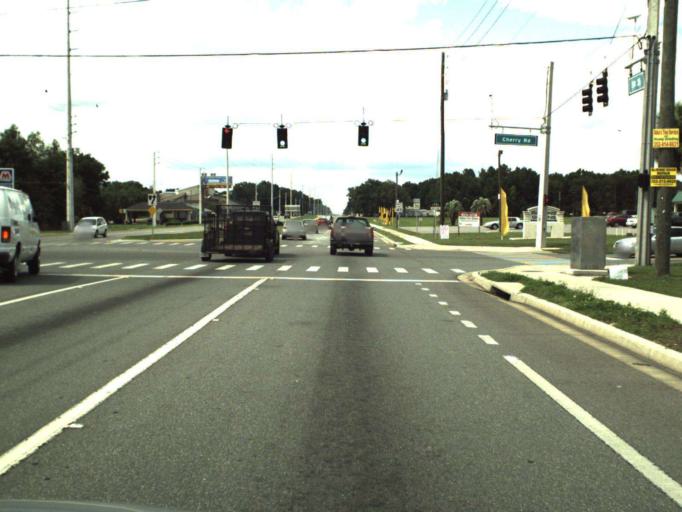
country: US
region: Florida
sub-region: Marion County
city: Silver Springs Shores
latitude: 29.1678
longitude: -82.0535
